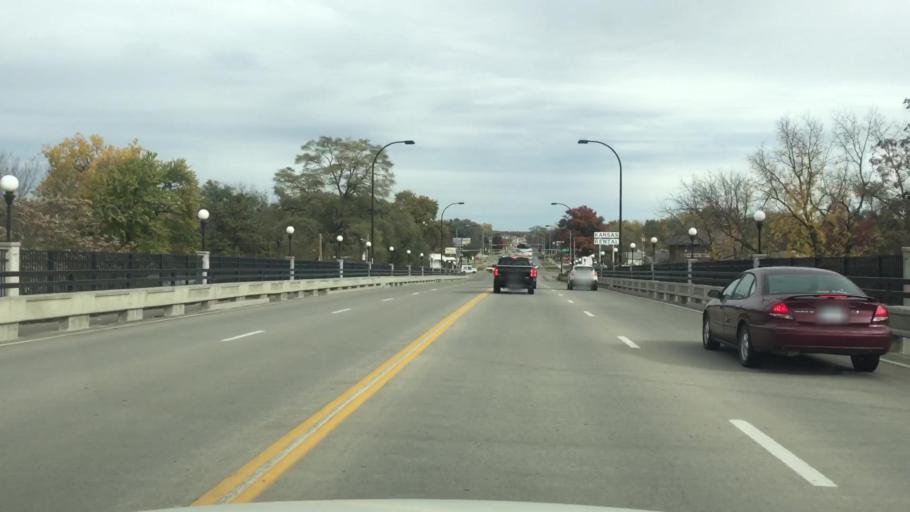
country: US
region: Kansas
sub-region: Shawnee County
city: Topeka
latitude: 39.0685
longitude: -95.6725
